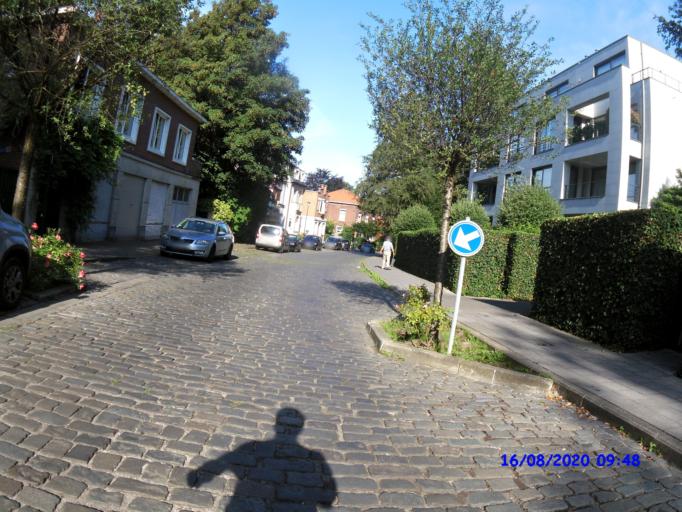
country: BE
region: Flanders
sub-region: Provincie Vlaams-Brabant
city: Drogenbos
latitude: 50.7960
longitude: 4.3396
